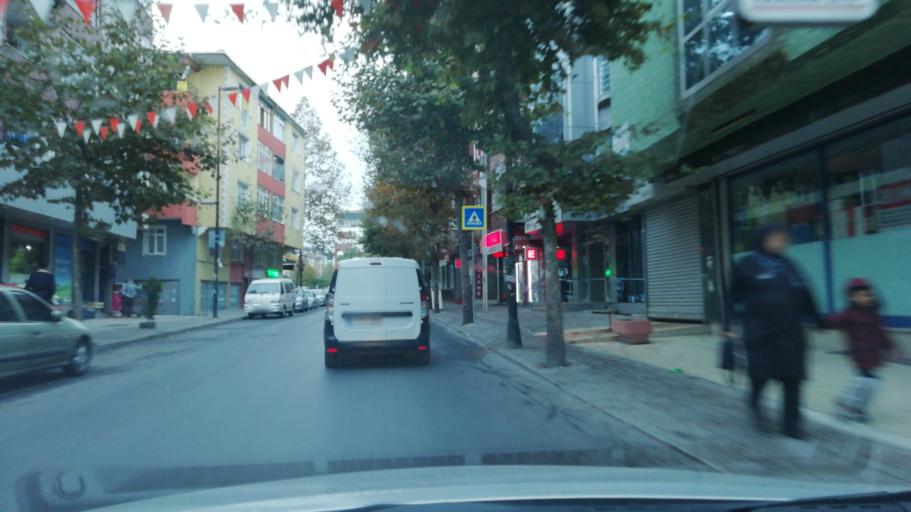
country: TR
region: Istanbul
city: Bahcelievler
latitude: 41.0182
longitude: 28.8327
